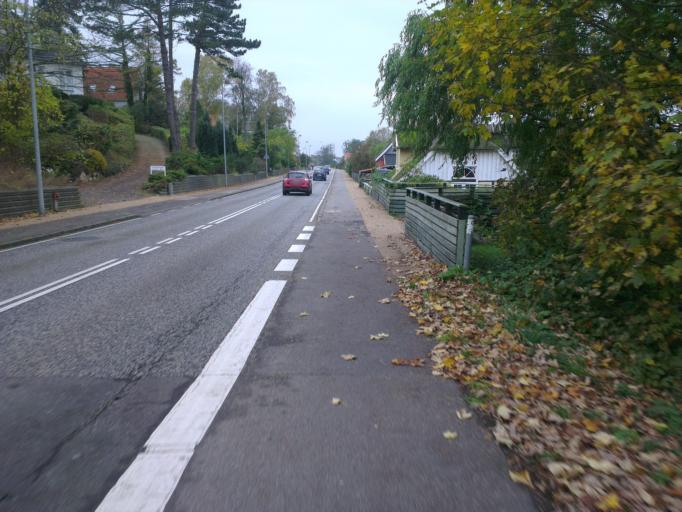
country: DK
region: Capital Region
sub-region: Frederikssund Kommune
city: Jaegerspris
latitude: 55.8551
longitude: 12.0129
